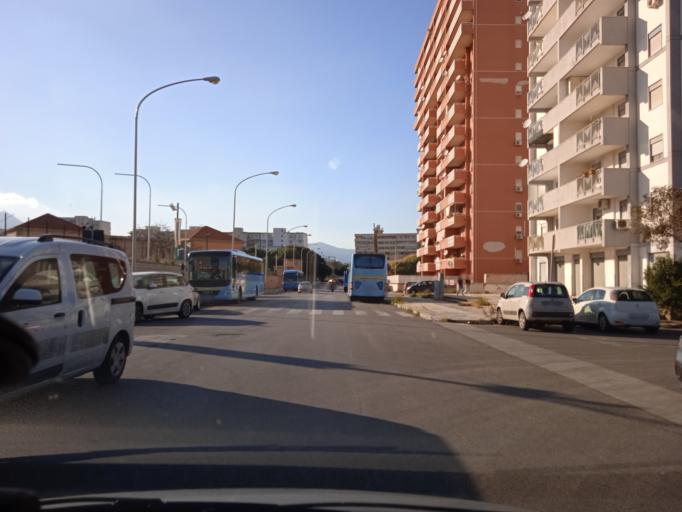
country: IT
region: Sicily
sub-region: Palermo
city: Ciaculli
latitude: 38.1064
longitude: 13.3805
